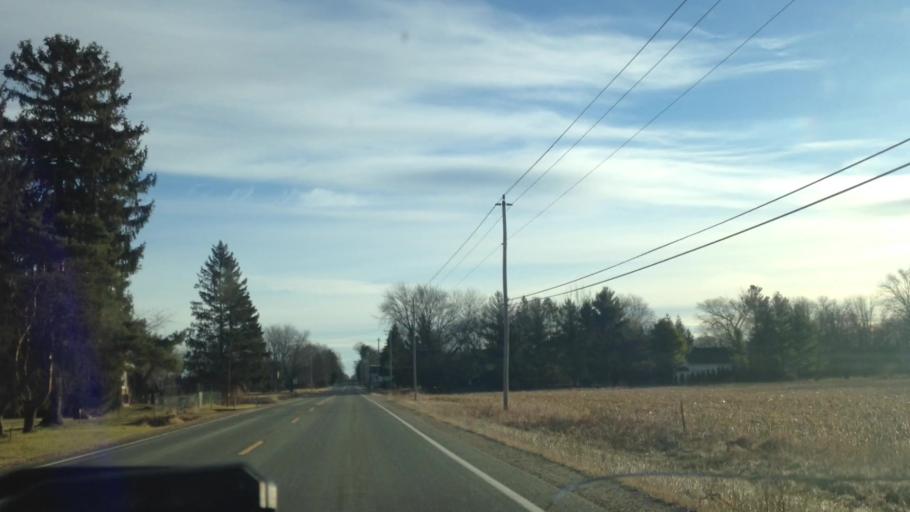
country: US
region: Wisconsin
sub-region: Washington County
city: Germantown
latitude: 43.2941
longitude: -88.1019
